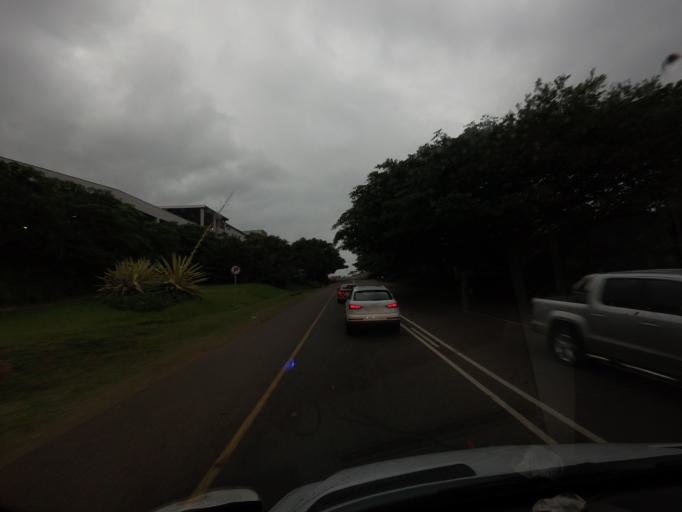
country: ZA
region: KwaZulu-Natal
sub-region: iLembe District Municipality
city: Ballitoville
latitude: -29.5301
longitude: 31.1996
